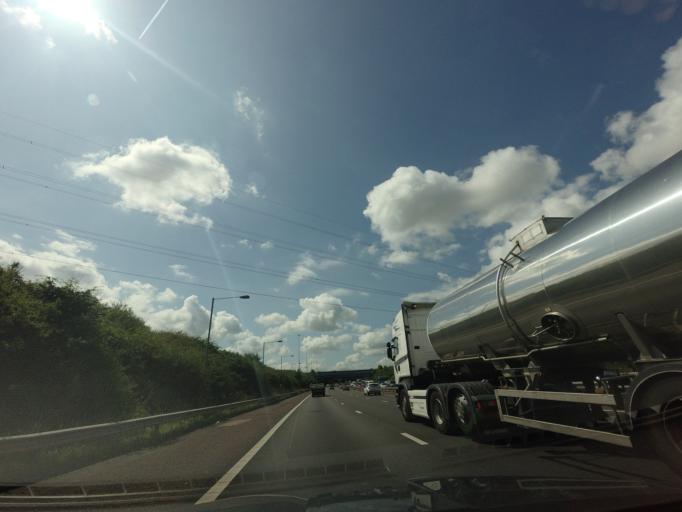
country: GB
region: England
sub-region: Lancashire
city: Clayton-le-Woods
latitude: 53.7179
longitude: -2.6579
